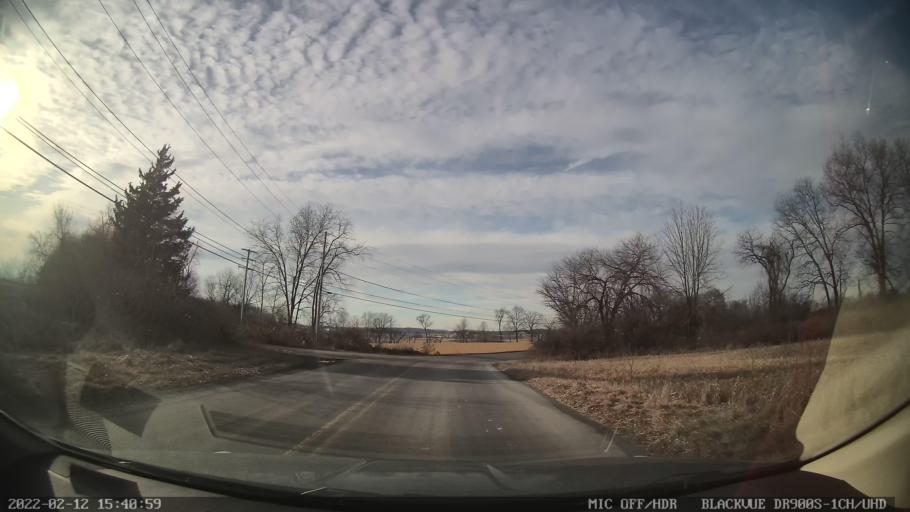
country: US
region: Pennsylvania
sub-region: Berks County
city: Topton
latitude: 40.5181
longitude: -75.7305
